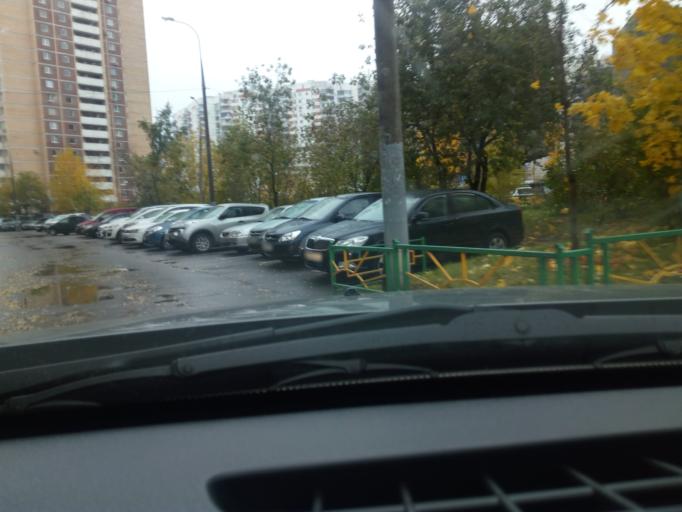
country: RU
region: Moskovskaya
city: Reutov
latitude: 55.7382
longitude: 37.8602
